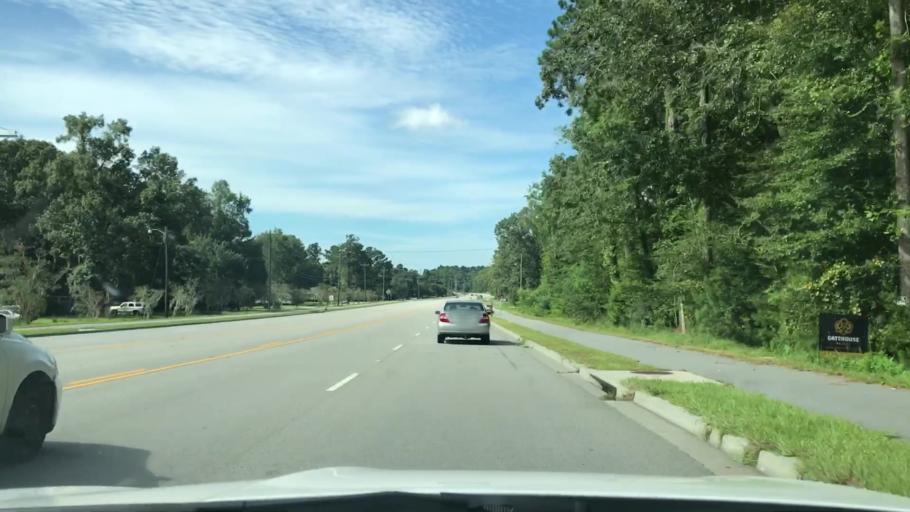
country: US
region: South Carolina
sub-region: Dorchester County
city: Centerville
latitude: 32.9820
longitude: -80.1949
